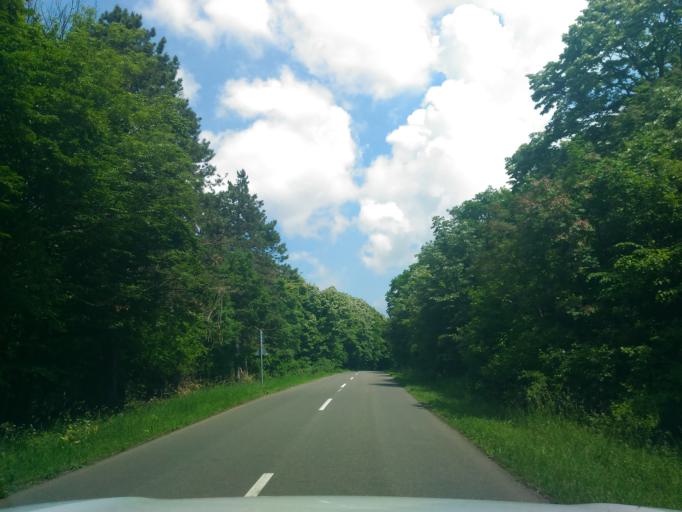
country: HU
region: Baranya
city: Pecs
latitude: 46.1133
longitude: 18.1979
